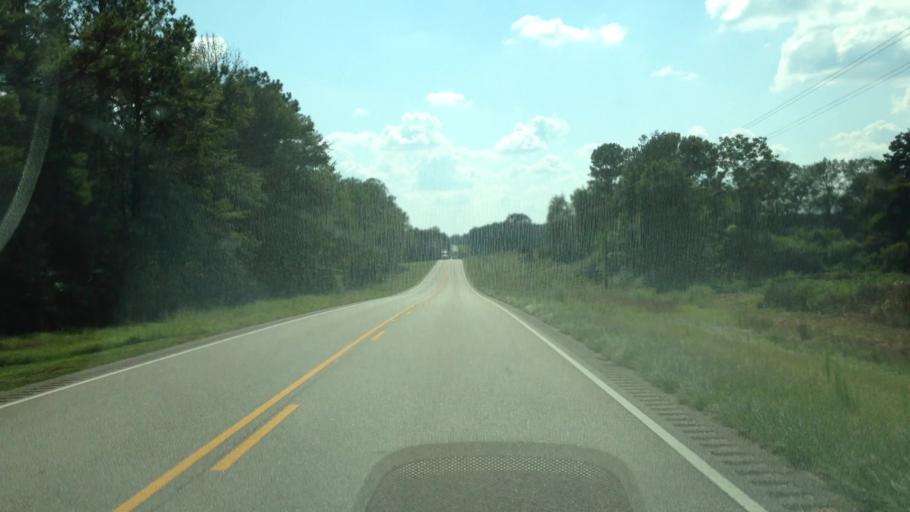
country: US
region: Alabama
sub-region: Covington County
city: Florala
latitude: 31.0414
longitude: -86.5961
